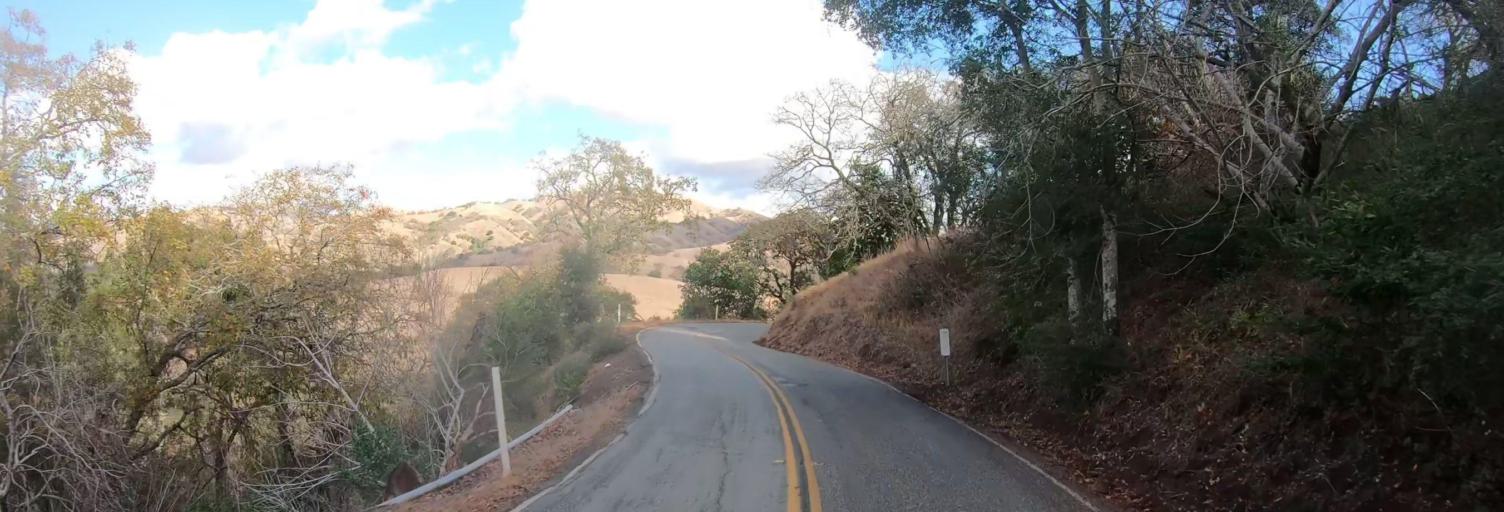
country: US
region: California
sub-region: Santa Clara County
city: East Foothills
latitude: 37.3535
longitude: -121.7393
